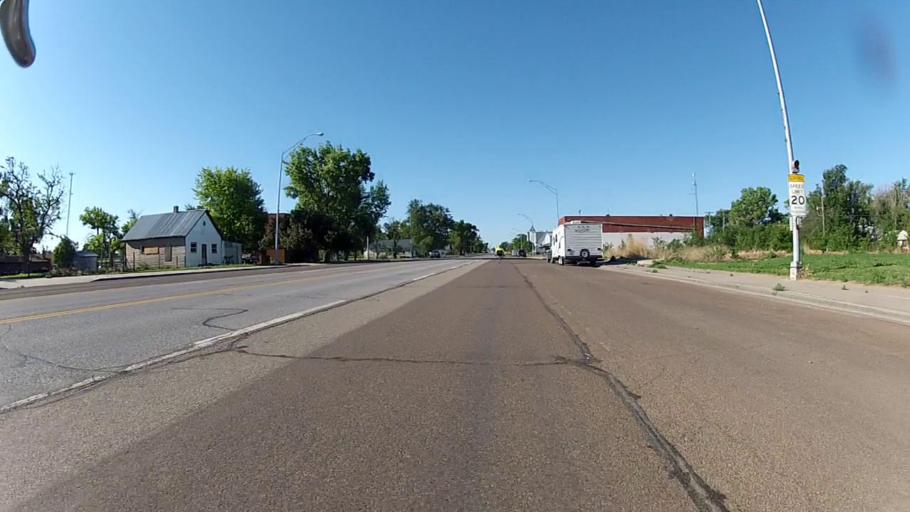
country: US
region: Kansas
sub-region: Ford County
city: Dodge City
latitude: 37.6393
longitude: -99.7539
